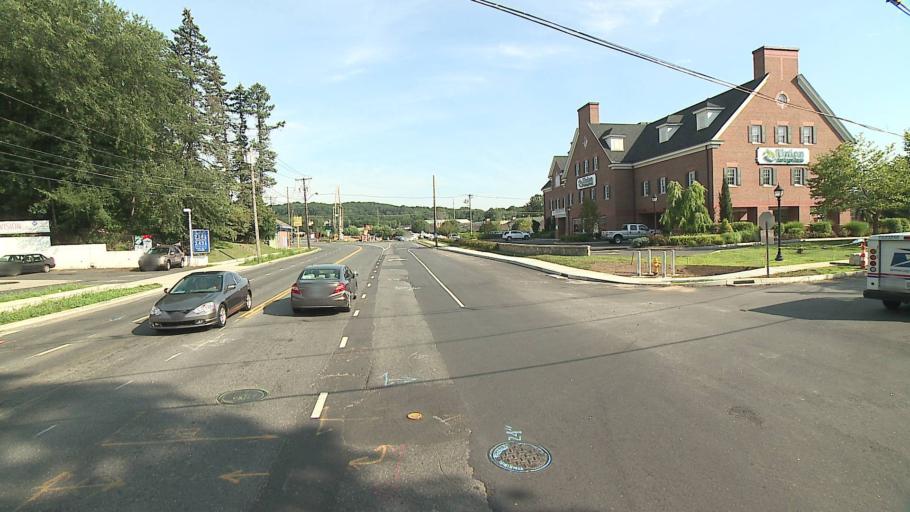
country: US
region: Connecticut
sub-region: Fairfield County
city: Danbury
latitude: 41.4110
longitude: -73.4554
